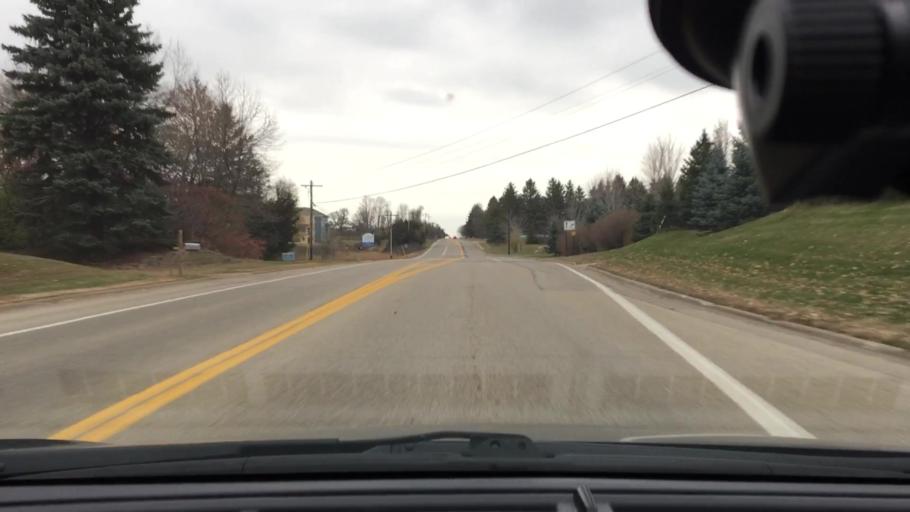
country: US
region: Minnesota
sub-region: Hennepin County
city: Corcoran
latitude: 45.0679
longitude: -93.5221
